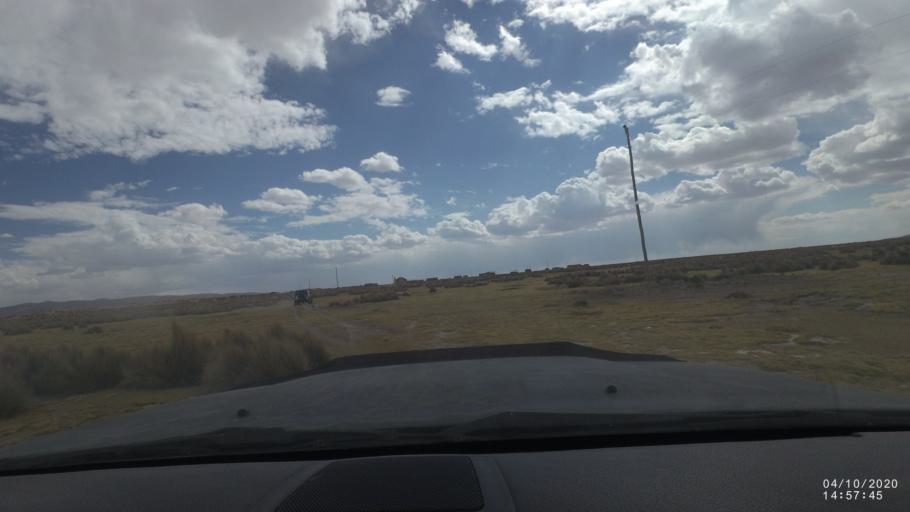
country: BO
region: Oruro
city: Poopo
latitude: -18.6856
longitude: -67.5196
